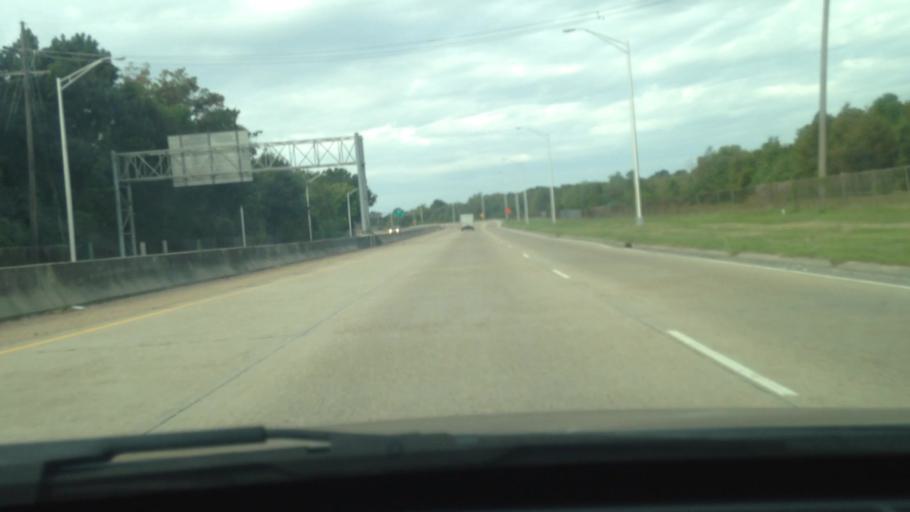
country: US
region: Louisiana
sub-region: Jefferson Parish
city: Elmwood
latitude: 29.9690
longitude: -90.1933
